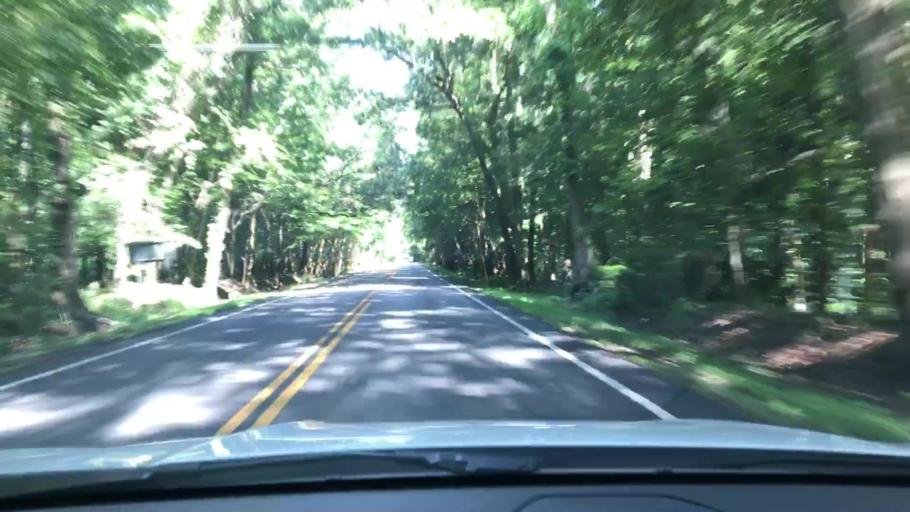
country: US
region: South Carolina
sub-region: Berkeley County
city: Hanahan
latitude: 32.8720
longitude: -80.0915
